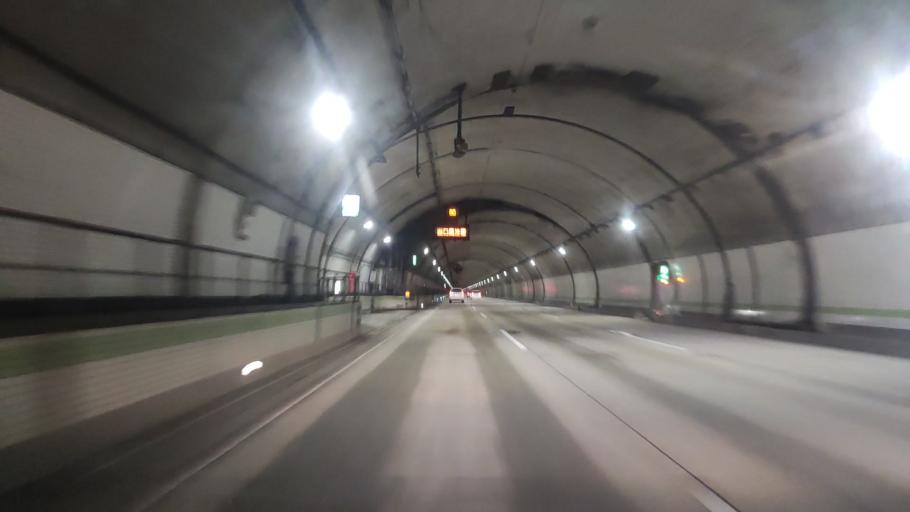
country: JP
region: Hyogo
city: Akashi
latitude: 34.6501
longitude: 135.0580
